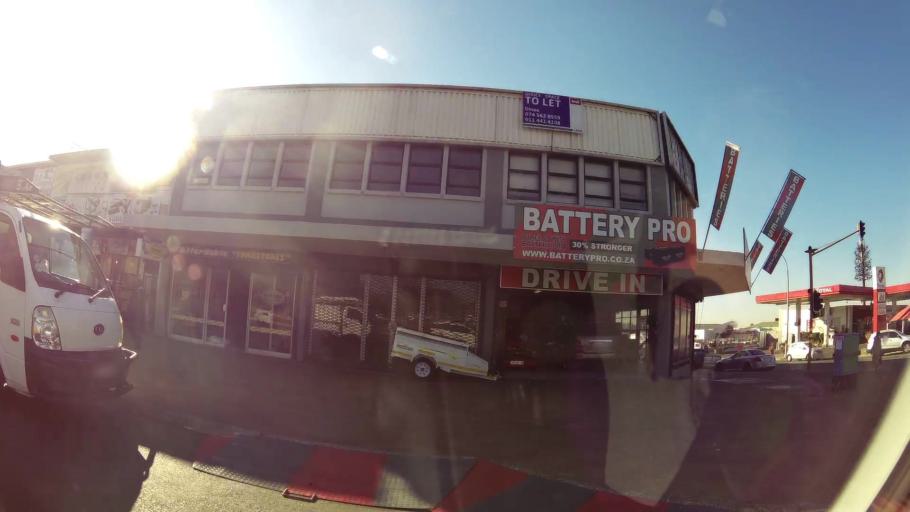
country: ZA
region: Gauteng
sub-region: Ekurhuleni Metropolitan Municipality
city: Germiston
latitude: -26.2709
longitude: 28.1221
